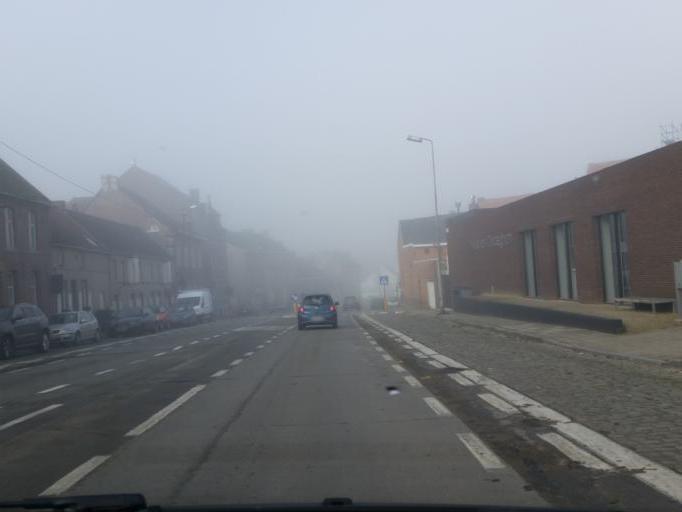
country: BE
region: Flanders
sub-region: Provincie Oost-Vlaanderen
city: Wetteren
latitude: 50.9566
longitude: 3.9025
